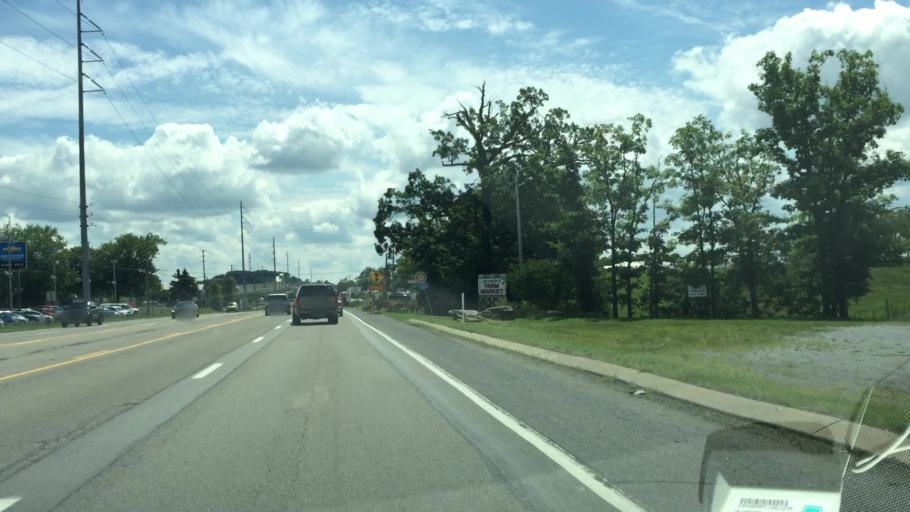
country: US
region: Pennsylvania
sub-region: Butler County
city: Zelienople
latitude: 40.7465
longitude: -80.1144
